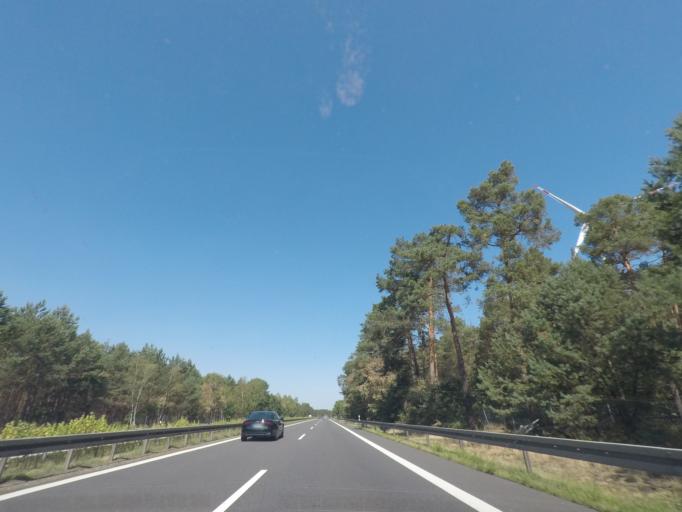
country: DE
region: Brandenburg
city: Bronkow
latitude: 51.7302
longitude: 13.8735
